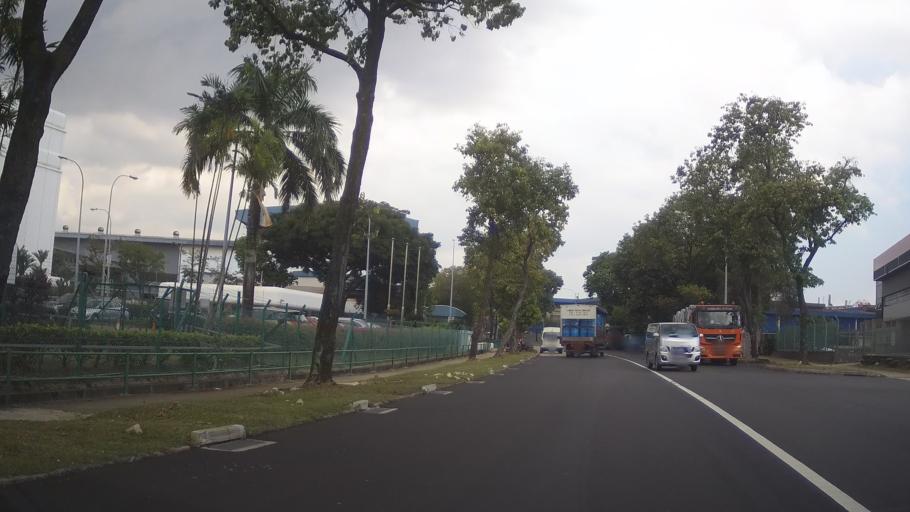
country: MY
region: Johor
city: Johor Bahru
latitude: 1.3062
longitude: 103.6626
